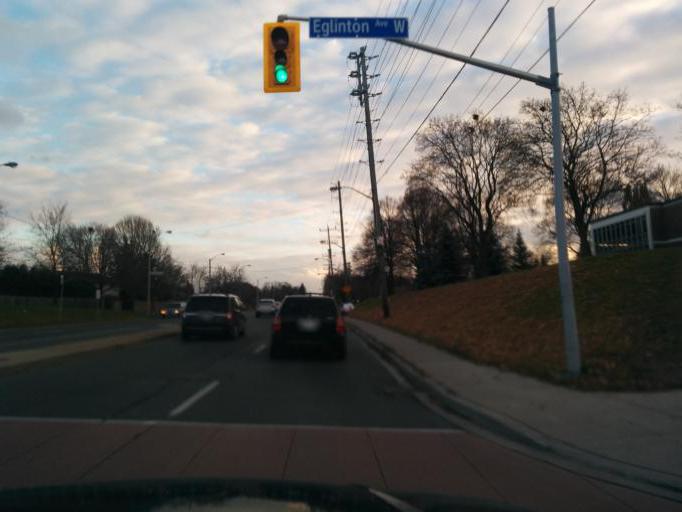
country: CA
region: Ontario
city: Etobicoke
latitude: 43.6798
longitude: -79.5391
